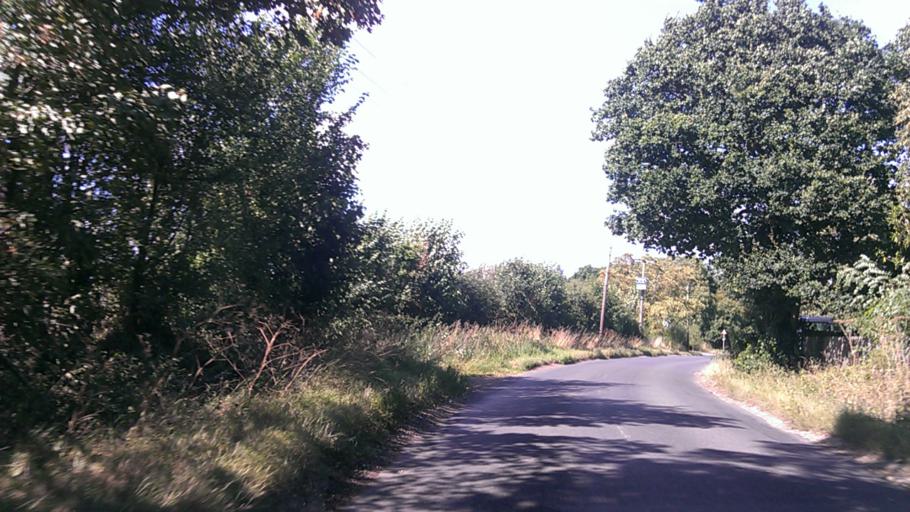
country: GB
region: England
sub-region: Essex
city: Layer de la Haye
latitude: 51.8561
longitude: 0.8822
